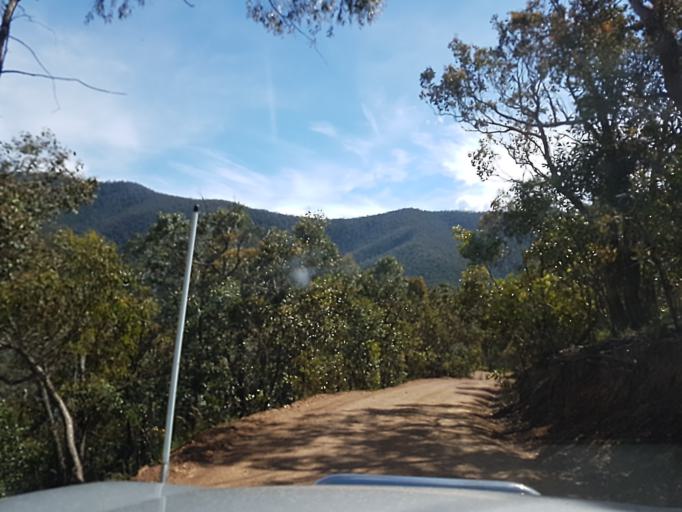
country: AU
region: Victoria
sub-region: Alpine
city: Mount Beauty
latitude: -37.3747
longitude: 147.0438
